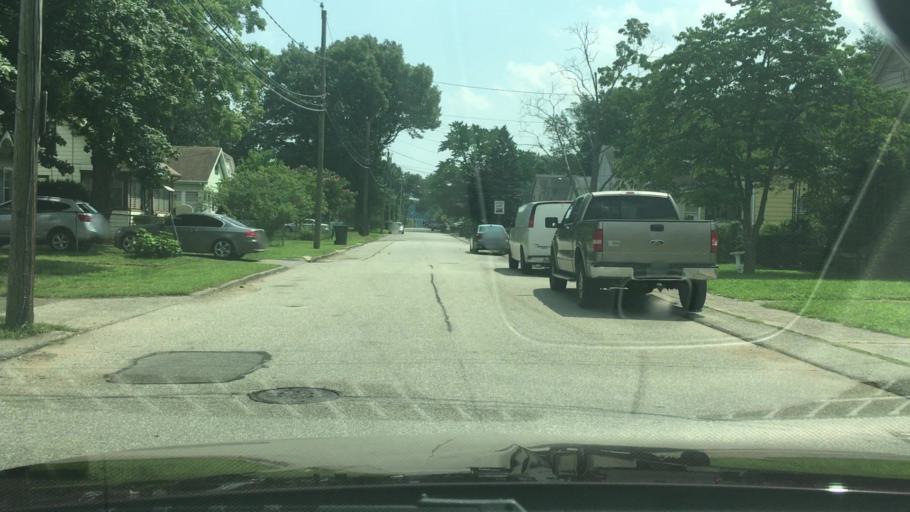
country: US
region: Connecticut
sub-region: Hartford County
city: East Hartford
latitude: 41.7616
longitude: -72.6318
